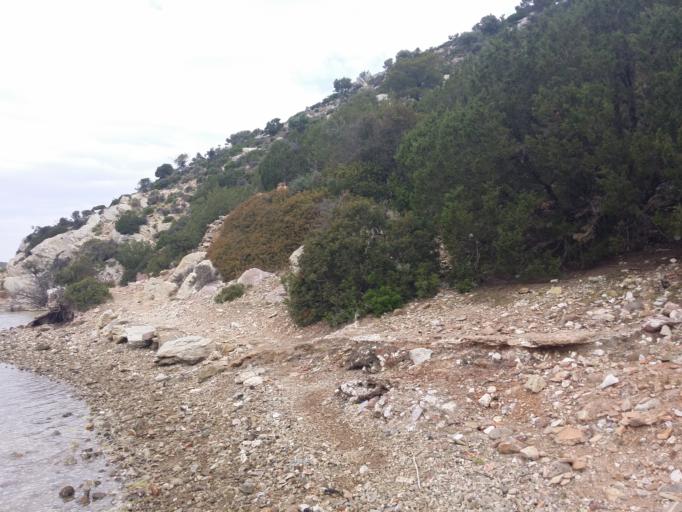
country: GR
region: Attica
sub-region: Nomos Piraios
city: Galatas
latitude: 37.5227
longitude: 23.4288
